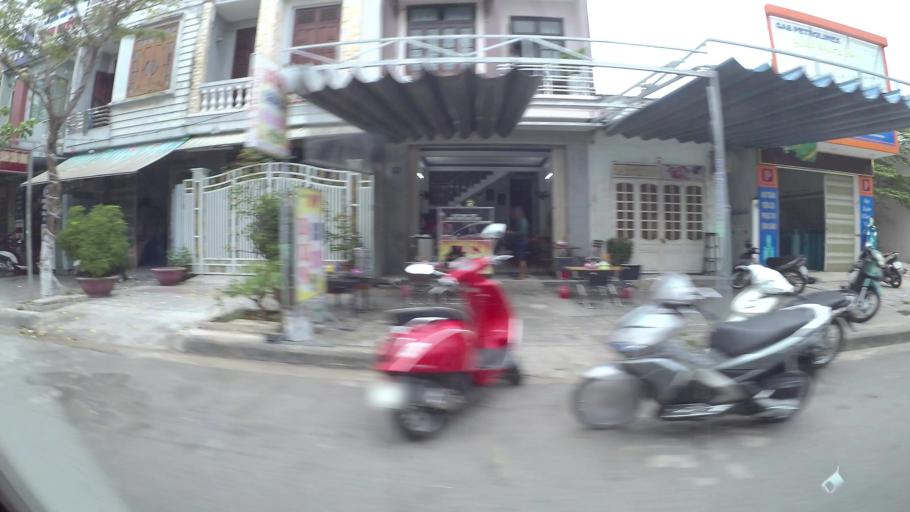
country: VN
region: Da Nang
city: Da Nang
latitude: 16.0886
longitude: 108.2373
